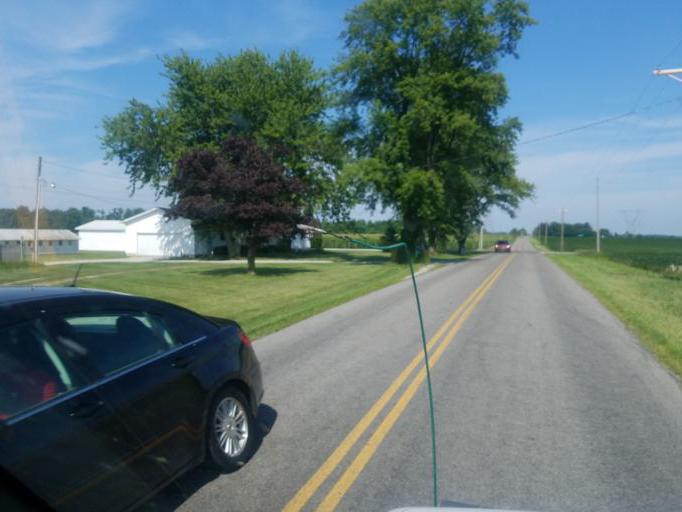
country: US
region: Ohio
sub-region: Shelby County
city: Jackson Center
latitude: 40.4976
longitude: -84.0748
